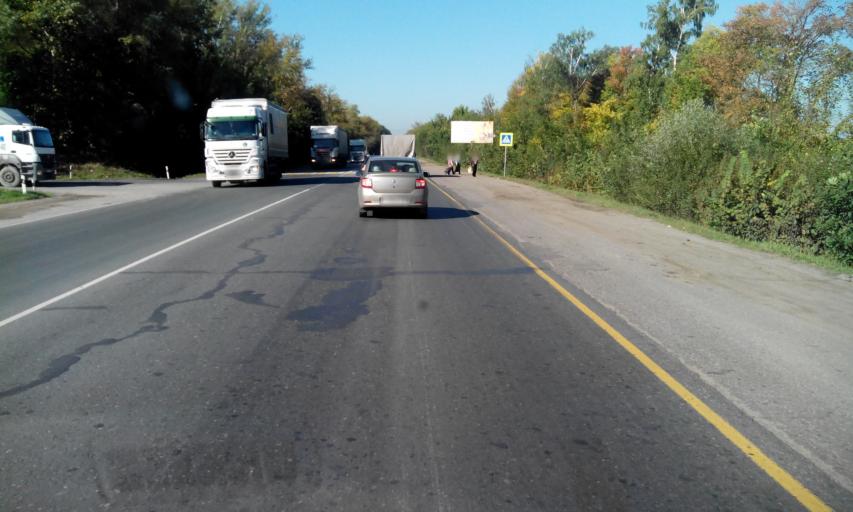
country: RU
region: Penza
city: Chemodanovka
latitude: 53.2214
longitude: 45.2251
